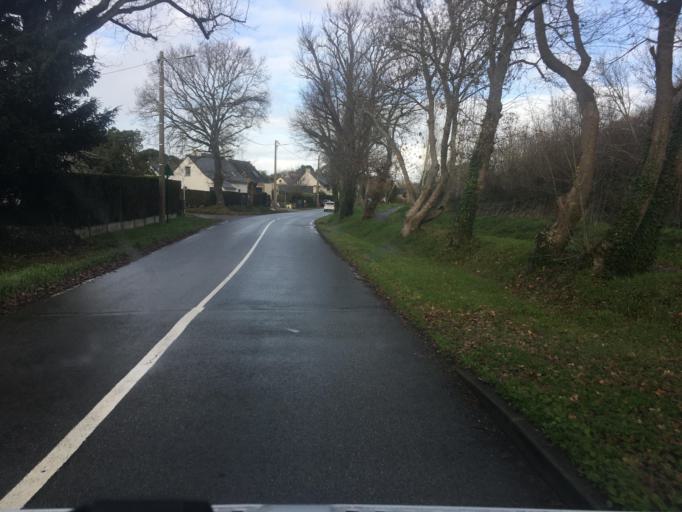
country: FR
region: Brittany
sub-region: Departement du Morbihan
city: Sarzeau
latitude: 47.5029
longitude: -2.7717
